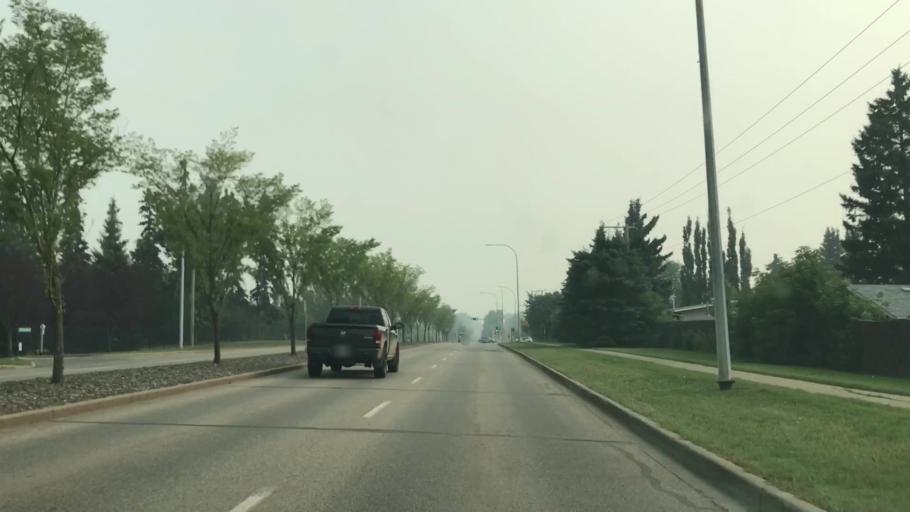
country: CA
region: Alberta
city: Sherwood Park
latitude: 53.5231
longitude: -113.3201
